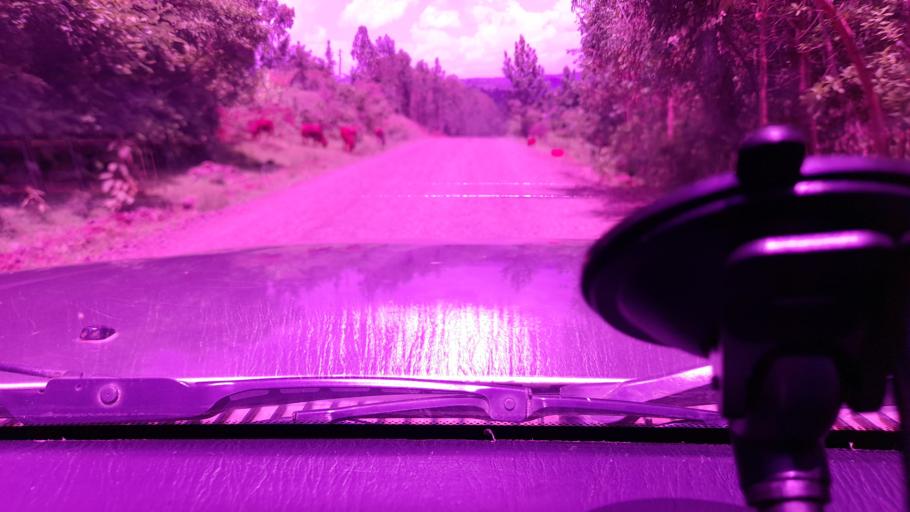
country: ET
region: Oromiya
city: Jima
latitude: 7.9931
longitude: 37.4796
